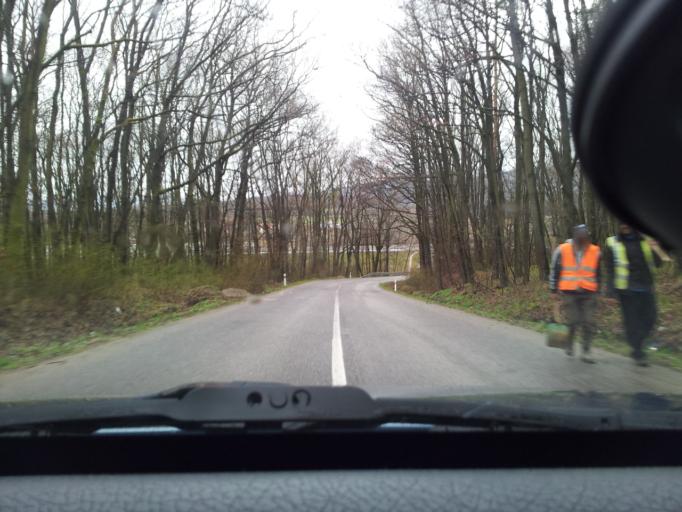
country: SK
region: Nitriansky
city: Tlmace
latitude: 48.3508
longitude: 18.4808
